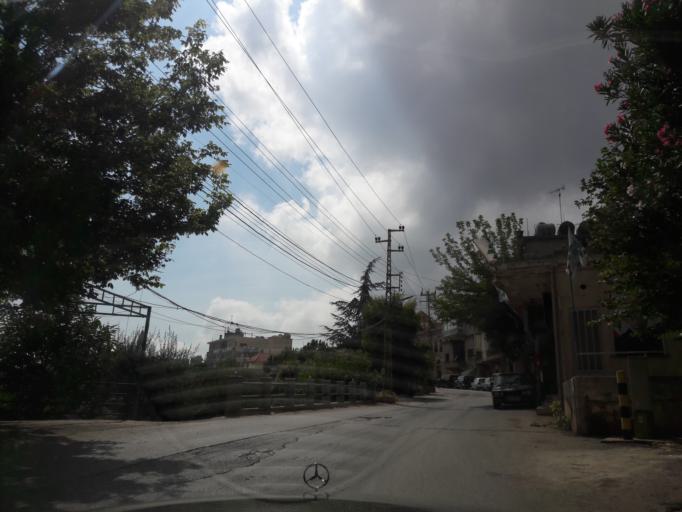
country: LB
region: Beqaa
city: Zahle
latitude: 33.9437
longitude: 35.7908
